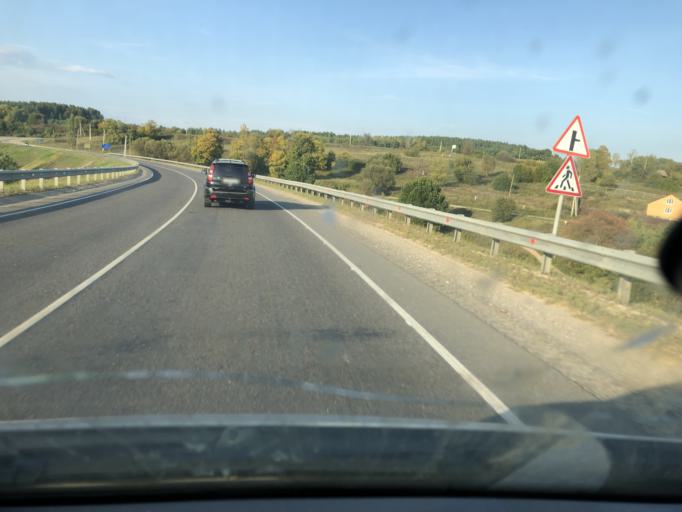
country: RU
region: Kaluga
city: Peremyshl'
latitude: 54.2940
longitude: 36.1787
